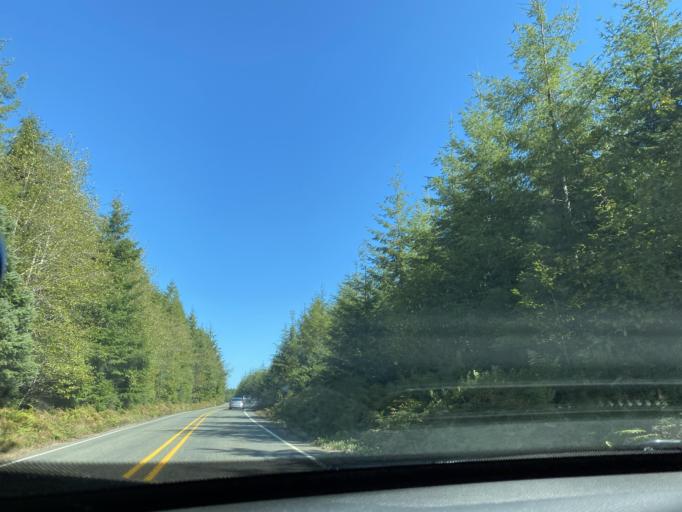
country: US
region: Washington
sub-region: Clallam County
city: Forks
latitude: 47.9371
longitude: -124.4694
